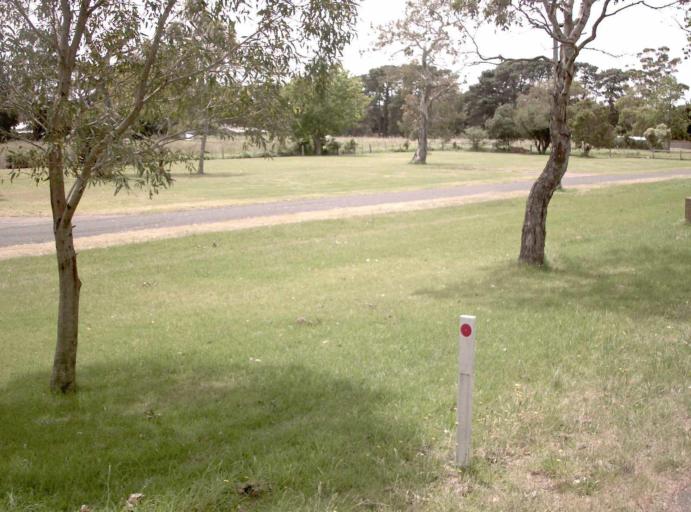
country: AU
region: Victoria
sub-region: Wellington
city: Sale
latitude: -38.1050
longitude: 147.1206
